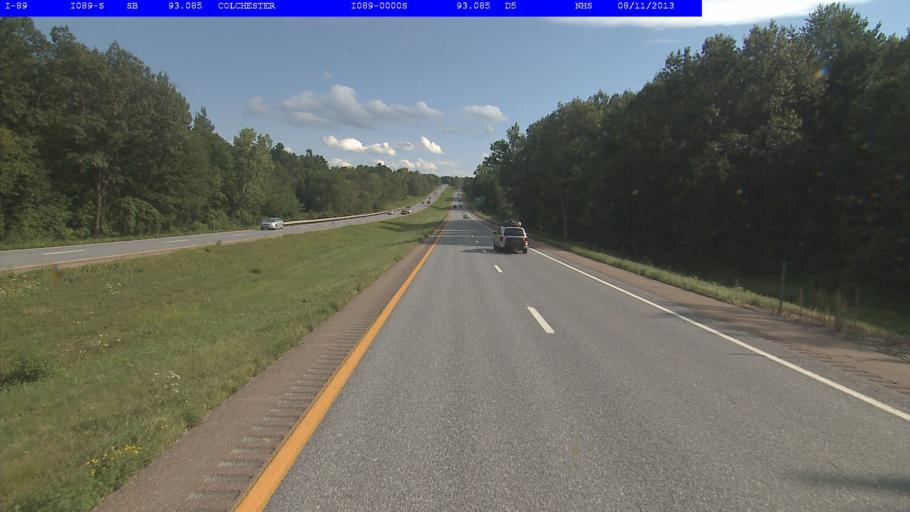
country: US
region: Vermont
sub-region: Chittenden County
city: Winooski
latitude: 44.5254
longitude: -73.1936
